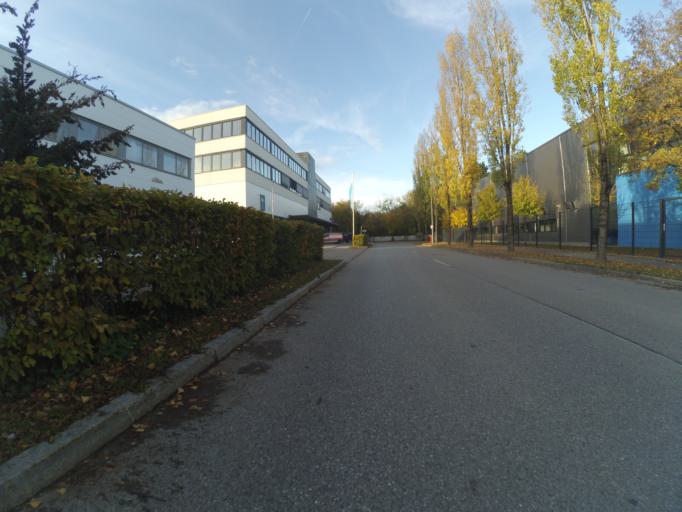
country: DE
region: Bavaria
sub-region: Upper Bavaria
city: Bogenhausen
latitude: 48.1960
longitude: 11.5901
